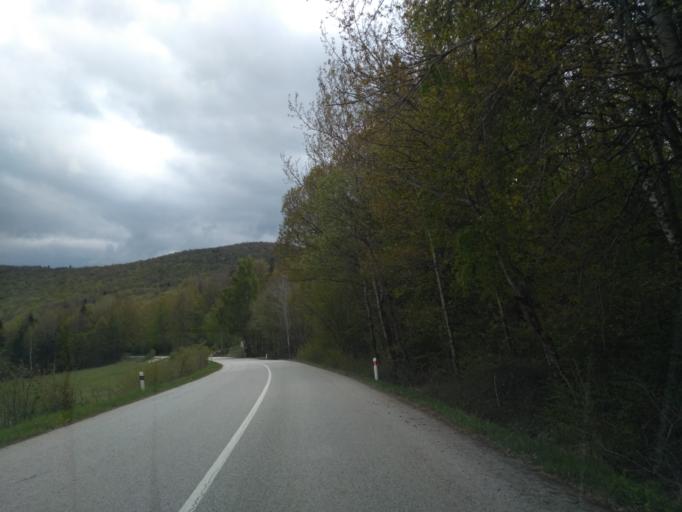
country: SK
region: Banskobystricky
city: Revuca
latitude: 48.6458
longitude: 20.3001
